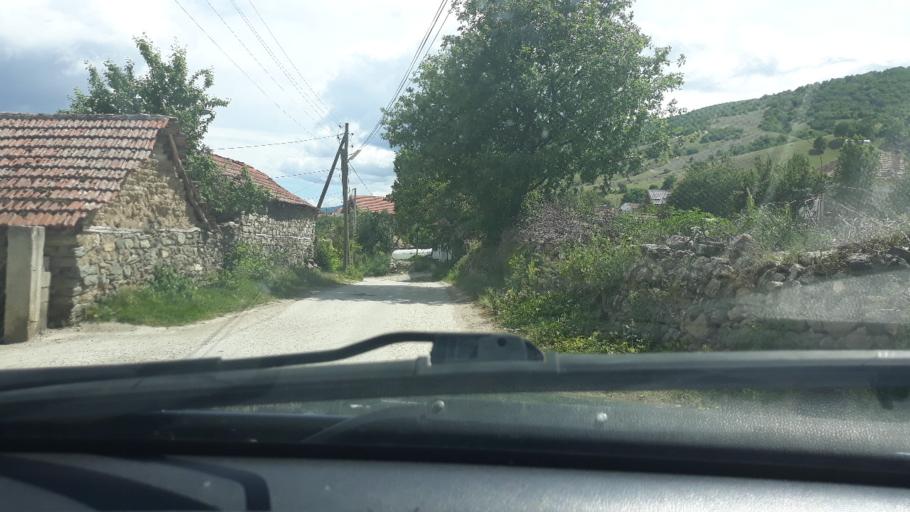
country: MK
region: Krivogastani
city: Krivogashtani
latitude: 41.3228
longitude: 21.3045
